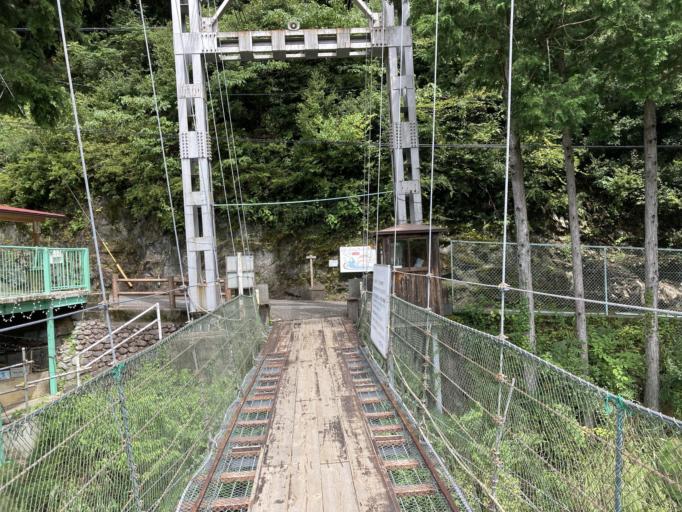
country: JP
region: Wakayama
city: Koya
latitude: 34.1032
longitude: 135.7626
